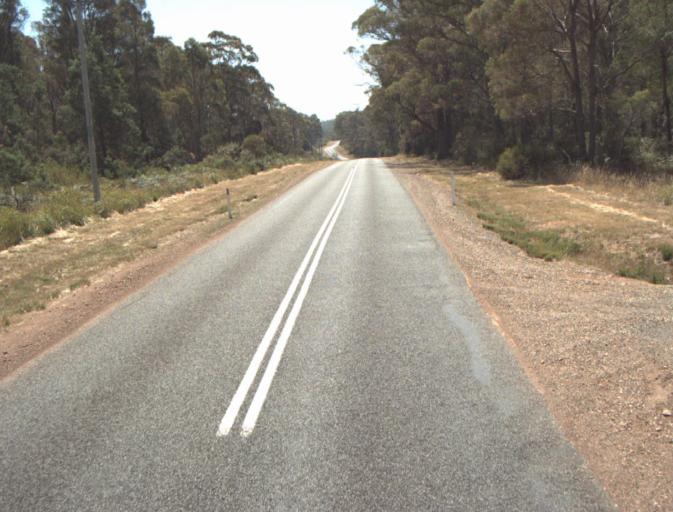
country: AU
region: Tasmania
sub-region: Launceston
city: Mayfield
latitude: -41.3083
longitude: 147.1337
